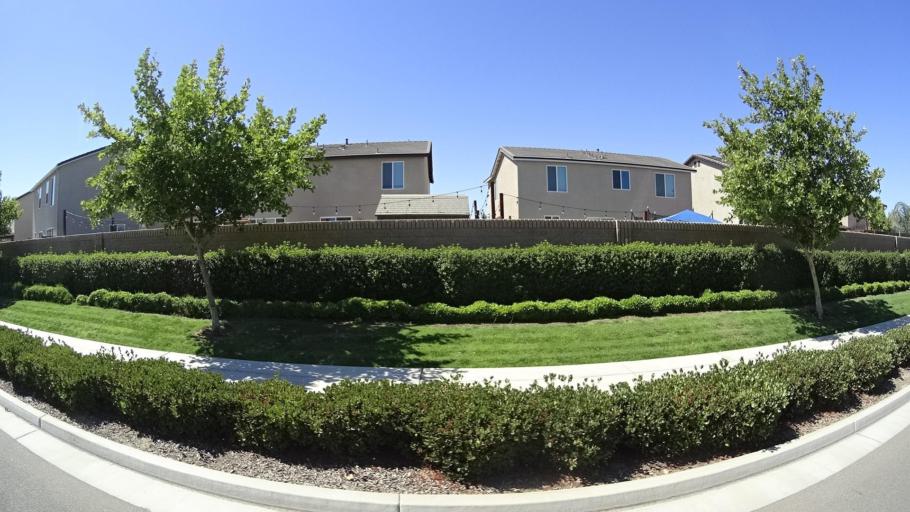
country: US
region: California
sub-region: Fresno County
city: Sunnyside
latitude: 36.7206
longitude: -119.6703
